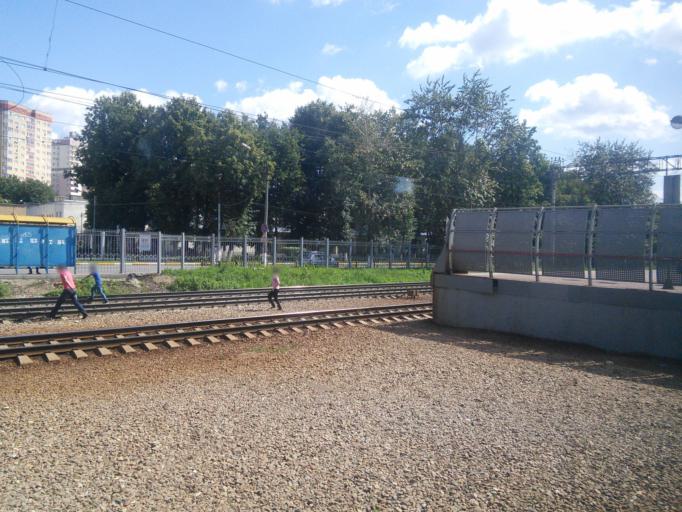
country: RU
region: Moskovskaya
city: Ramenskoye
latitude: 55.5735
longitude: 38.2048
